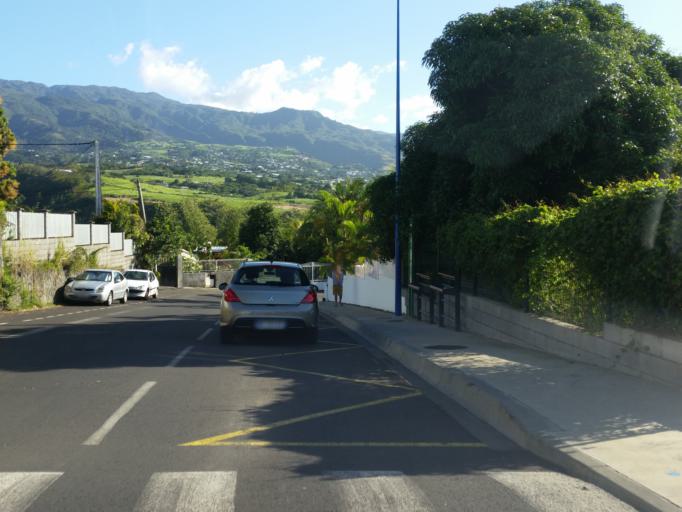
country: RE
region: Reunion
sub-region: Reunion
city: Sainte-Marie
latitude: -20.9193
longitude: 55.5147
